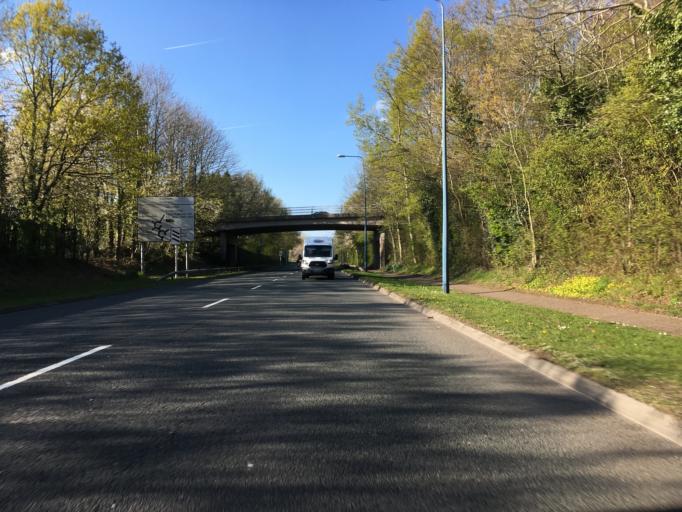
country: GB
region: Wales
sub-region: Torfaen County Borough
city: Cwmbran
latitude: 51.6412
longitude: -3.0217
